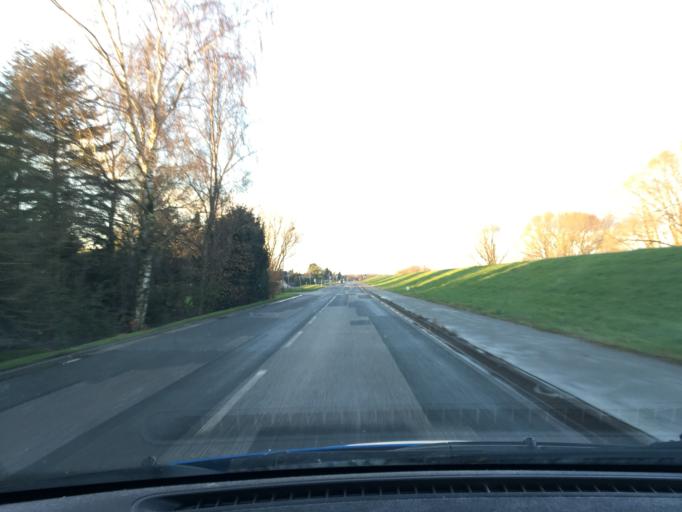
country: DE
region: Hamburg
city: Harburg
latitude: 53.4557
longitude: 10.0634
